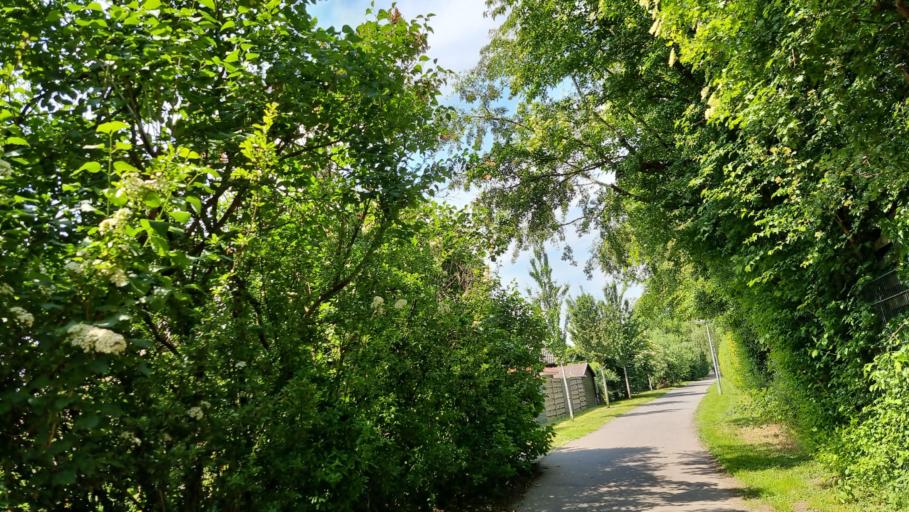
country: DE
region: Lower Saxony
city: Garbsen-Mitte
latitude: 52.4306
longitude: 9.6013
